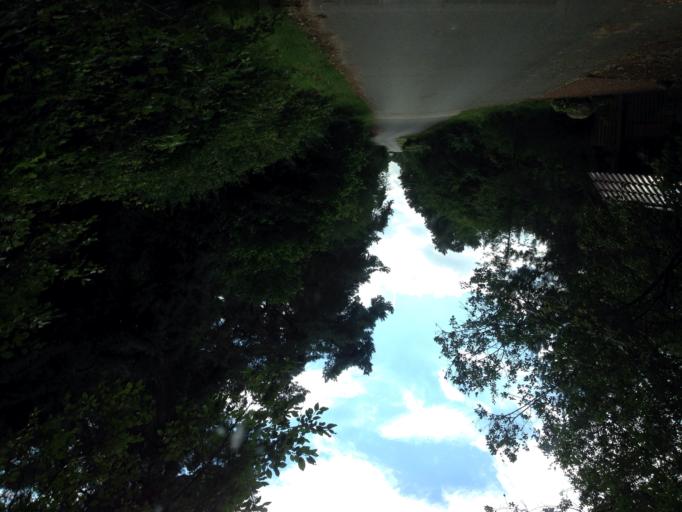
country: DE
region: Lower Saxony
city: Adendorf
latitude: 53.2959
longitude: 10.4396
